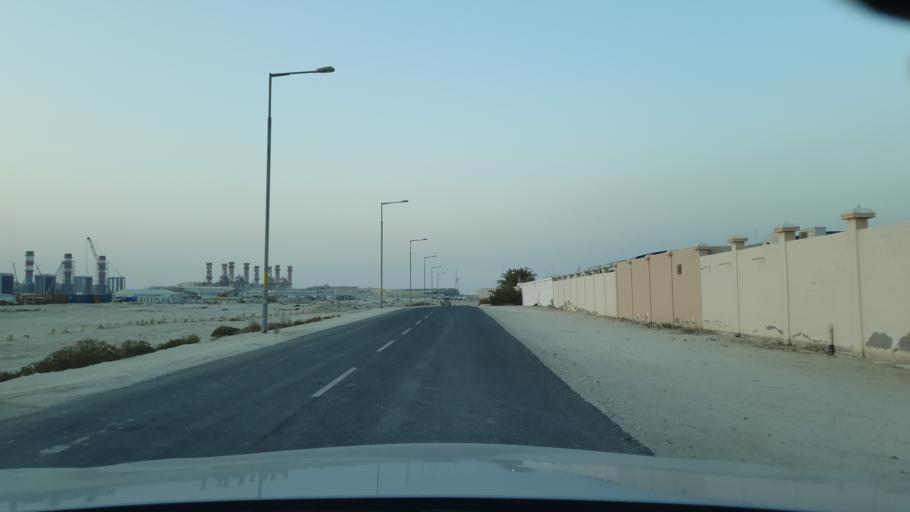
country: BH
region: Central Governorate
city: Dar Kulayb
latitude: 25.9602
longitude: 50.6113
